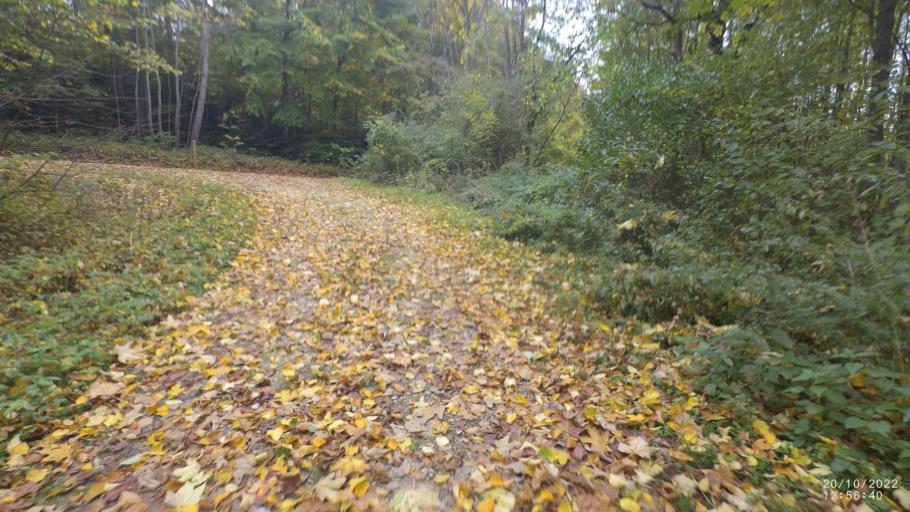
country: DE
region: Baden-Wuerttemberg
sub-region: Regierungsbezirk Stuttgart
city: Boll
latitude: 48.6177
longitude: 9.5924
